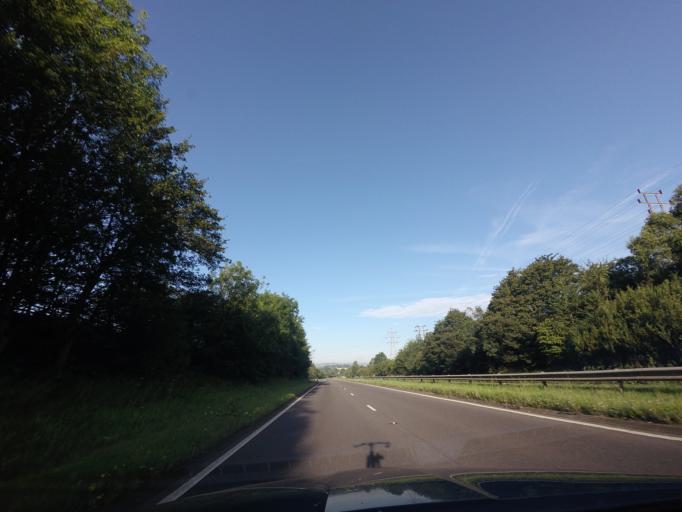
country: GB
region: England
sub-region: Derbyshire
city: Pilsley
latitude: 53.2007
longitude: -1.3497
